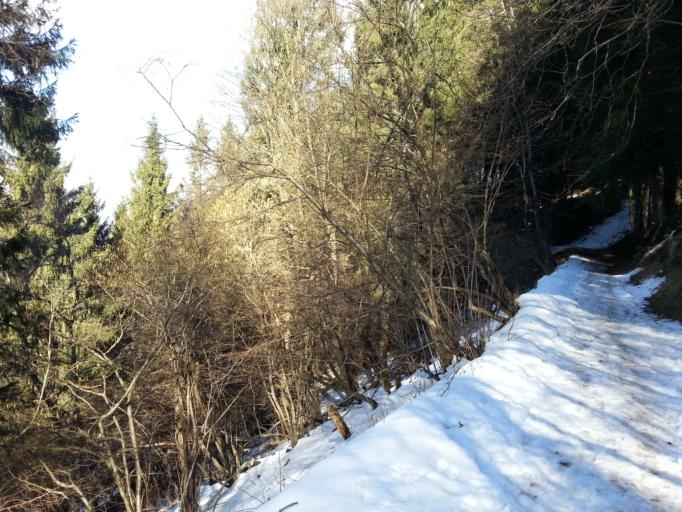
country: IT
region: Lombardy
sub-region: Provincia di Como
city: Lemna
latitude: 45.8356
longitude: 9.1453
